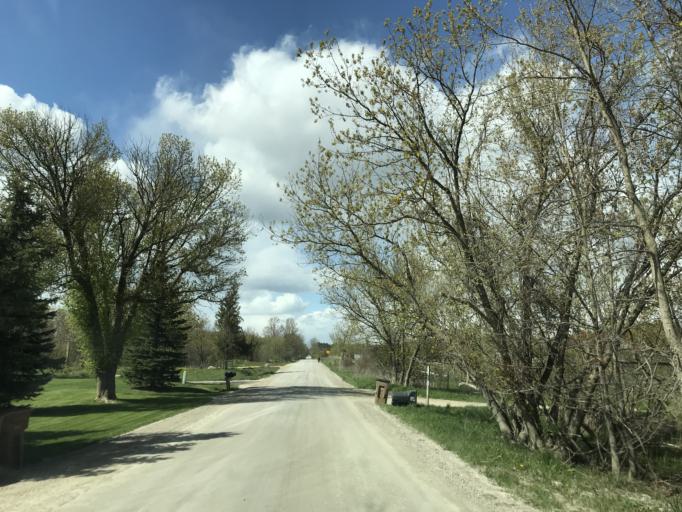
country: US
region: Michigan
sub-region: Oakland County
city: South Lyon
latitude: 42.3991
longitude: -83.6637
